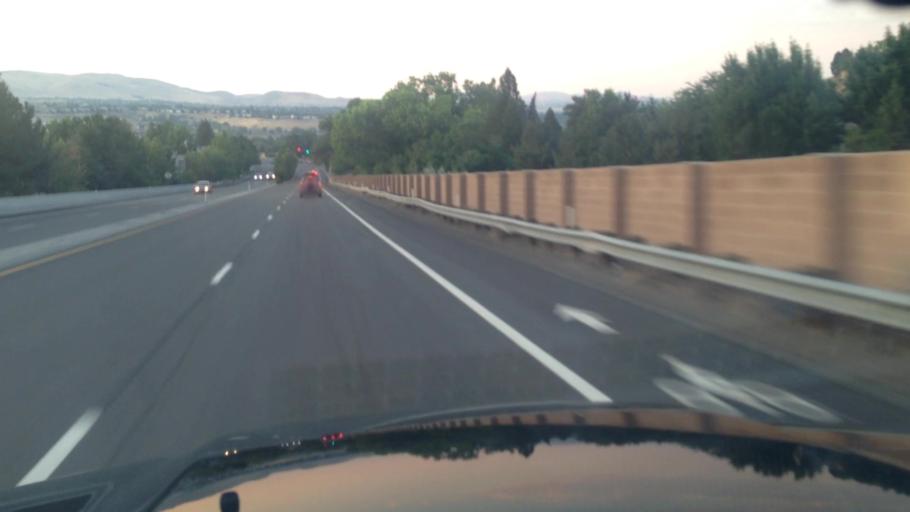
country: US
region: Nevada
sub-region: Washoe County
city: Reno
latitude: 39.4971
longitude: -119.8591
